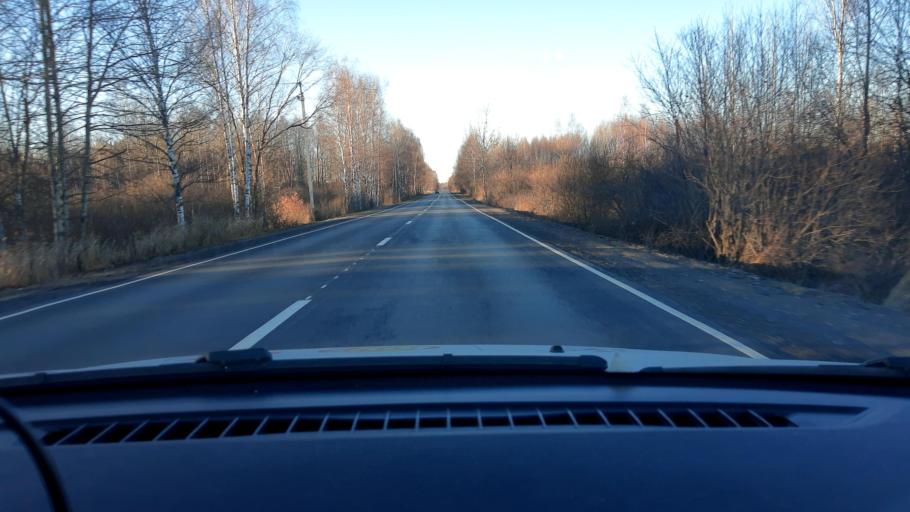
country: RU
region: Nizjnij Novgorod
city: Novaya Balakhna
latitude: 56.5623
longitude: 43.7266
